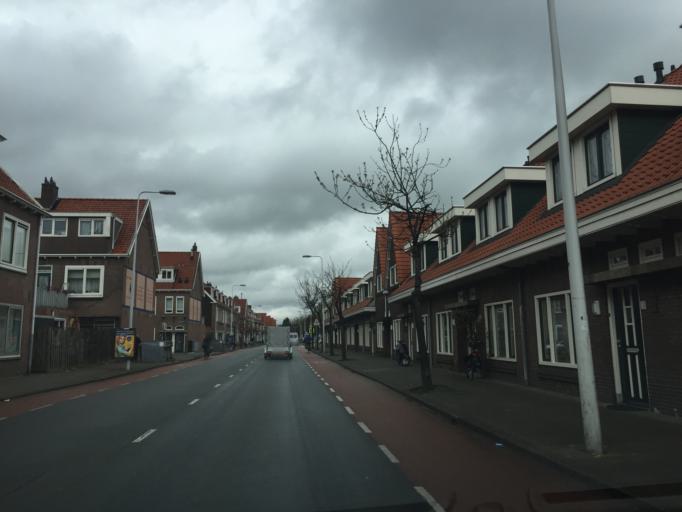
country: NL
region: South Holland
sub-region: Gemeente Leiderdorp
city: Leiderdorp
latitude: 52.1619
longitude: 4.5122
